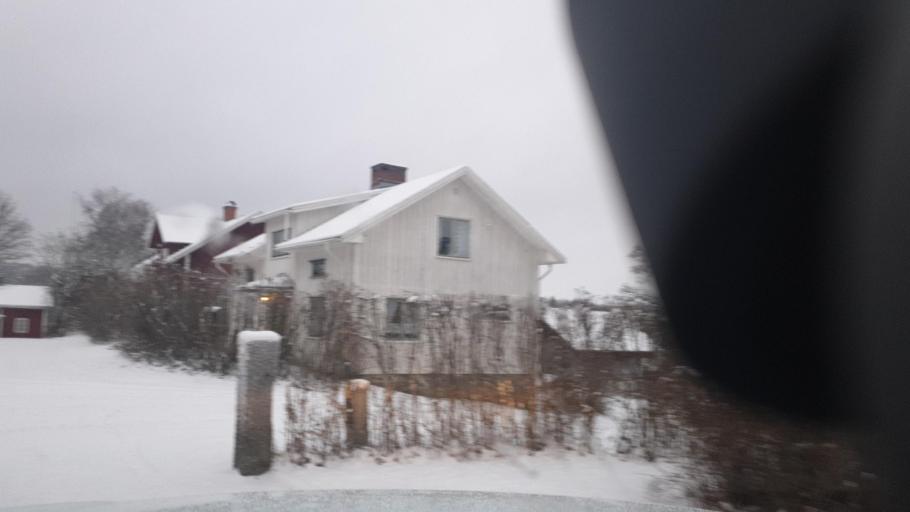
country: SE
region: Vaermland
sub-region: Eda Kommun
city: Amotfors
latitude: 59.7312
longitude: 12.1974
